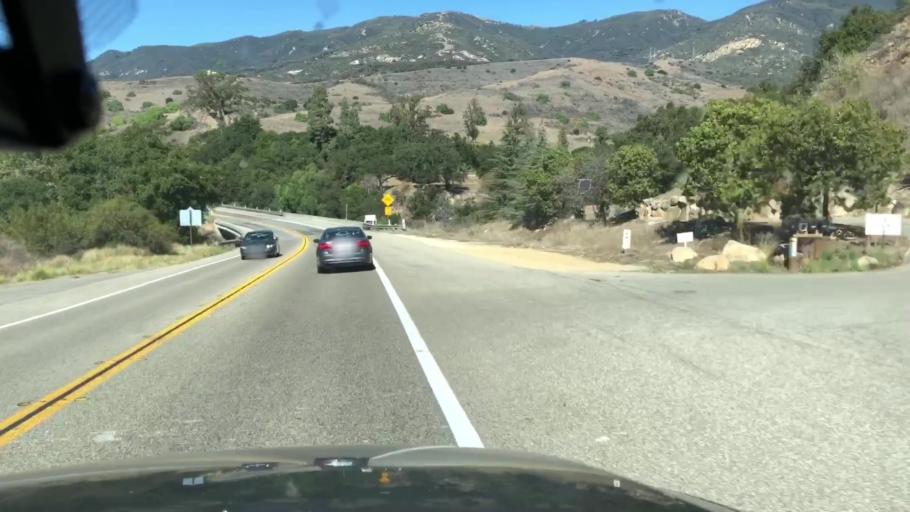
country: US
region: California
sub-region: Santa Barbara County
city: Mission Canyon
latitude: 34.4665
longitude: -119.7716
